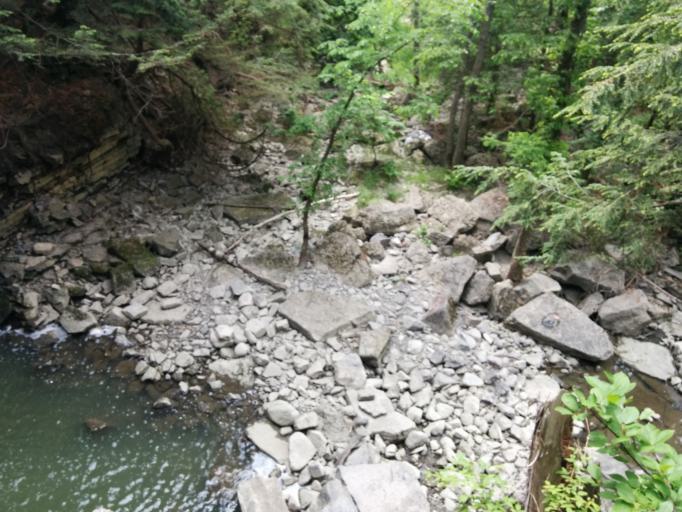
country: CA
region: Ontario
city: Clarence-Rockland
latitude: 45.4866
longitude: -75.4697
